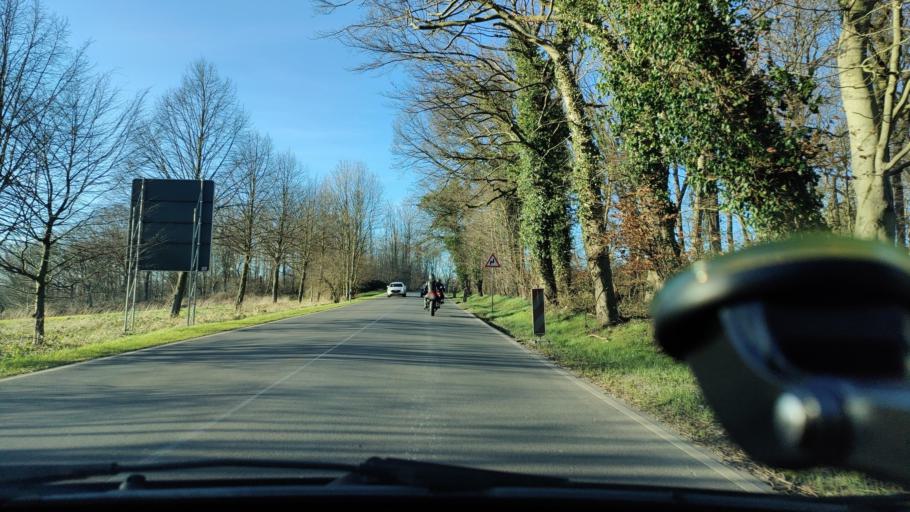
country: DE
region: North Rhine-Westphalia
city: Castrop-Rauxel
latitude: 51.5608
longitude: 7.2901
